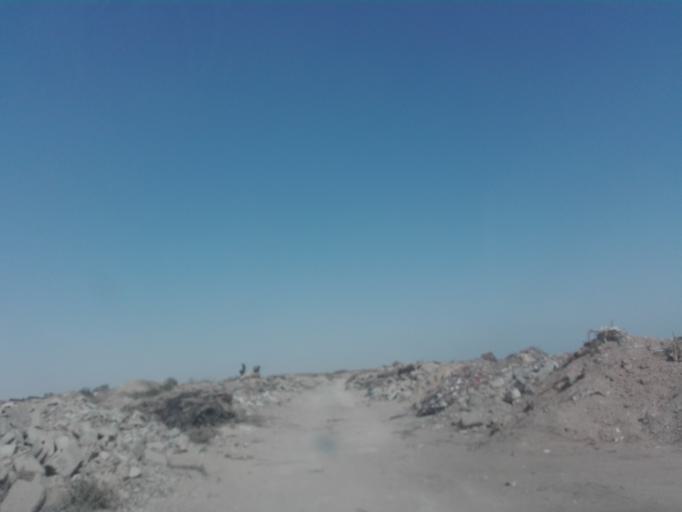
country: TN
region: Qabis
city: Gabes
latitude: 33.9616
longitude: 10.0663
